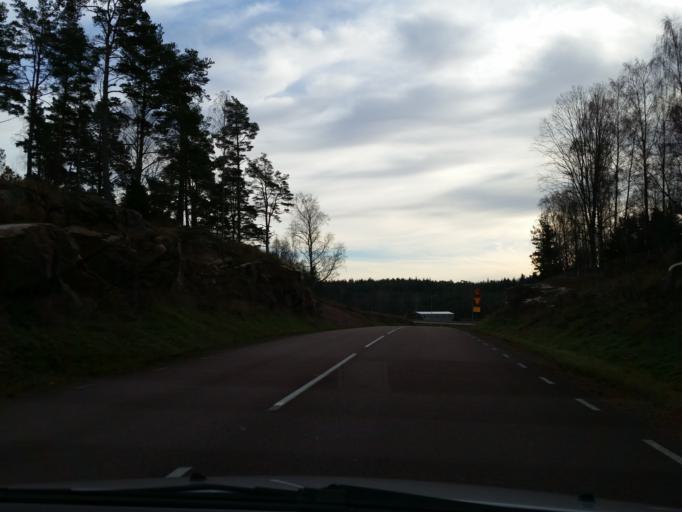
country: AX
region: Alands landsbygd
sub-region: Saltvik
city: Saltvik
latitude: 60.2479
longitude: 20.0402
